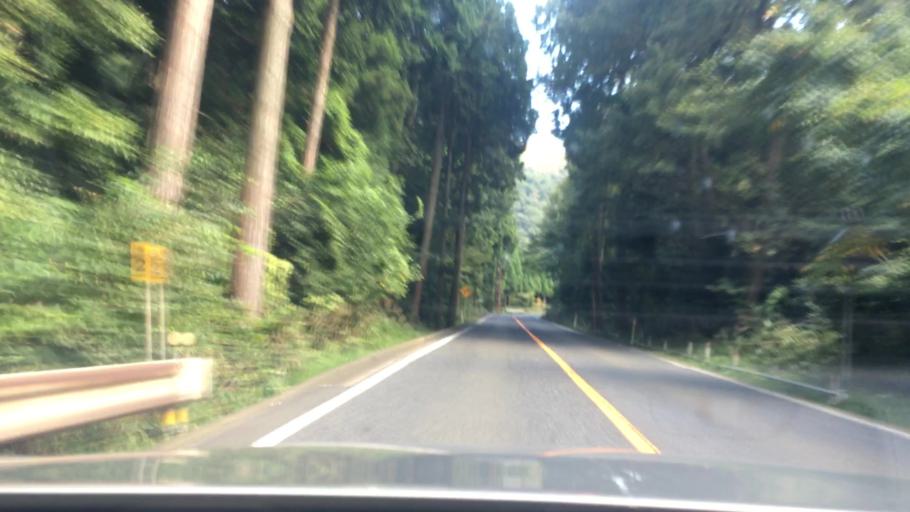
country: JP
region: Fukui
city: Tsuruga
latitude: 35.5863
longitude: 136.1022
